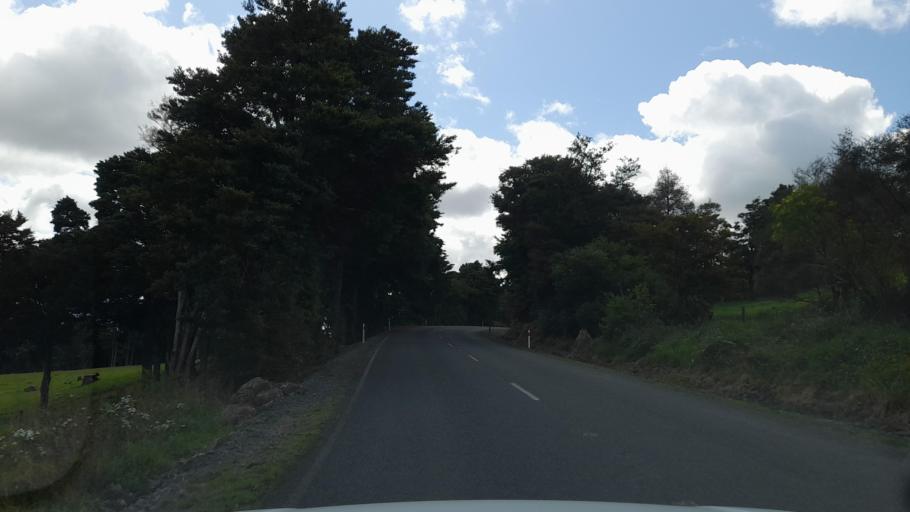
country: NZ
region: Northland
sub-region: Whangarei
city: Maungatapere
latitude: -35.7051
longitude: 174.0474
